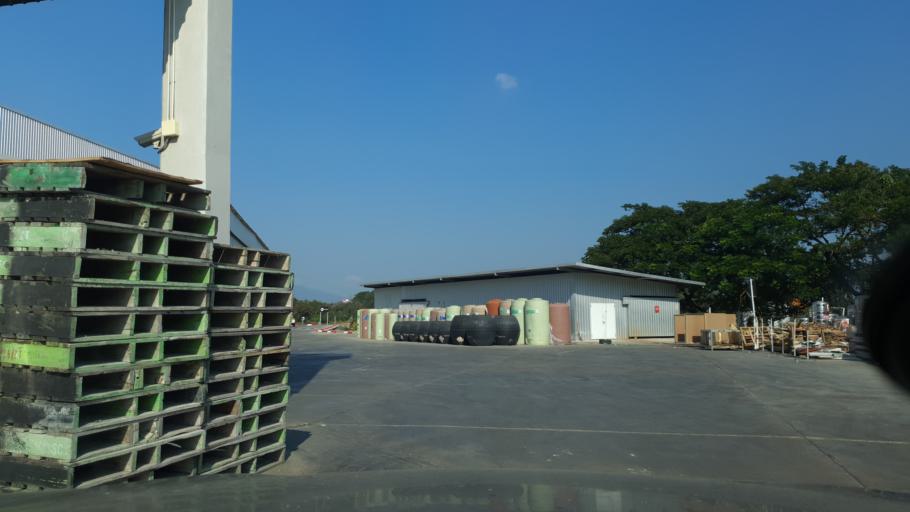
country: TH
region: Chiang Mai
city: Saraphi
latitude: 18.7216
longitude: 99.0448
